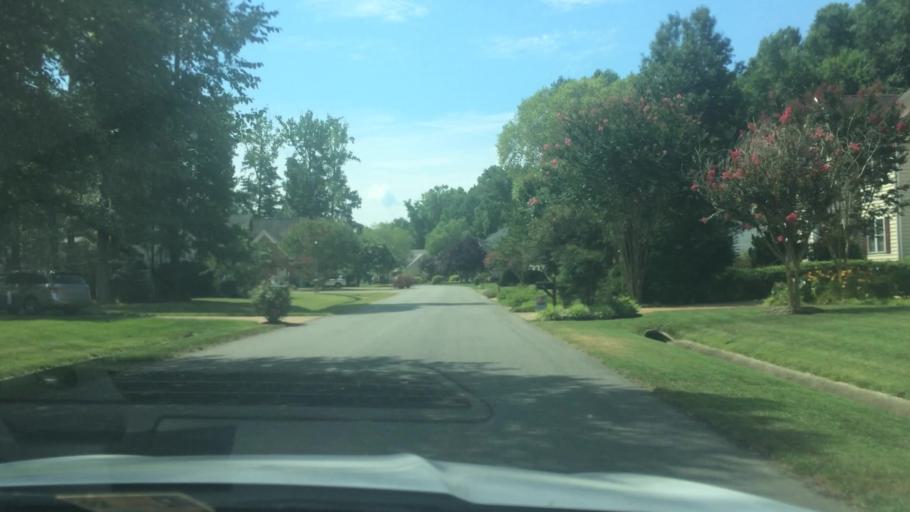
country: US
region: Virginia
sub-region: City of Poquoson
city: Poquoson
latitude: 37.1112
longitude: -76.4234
